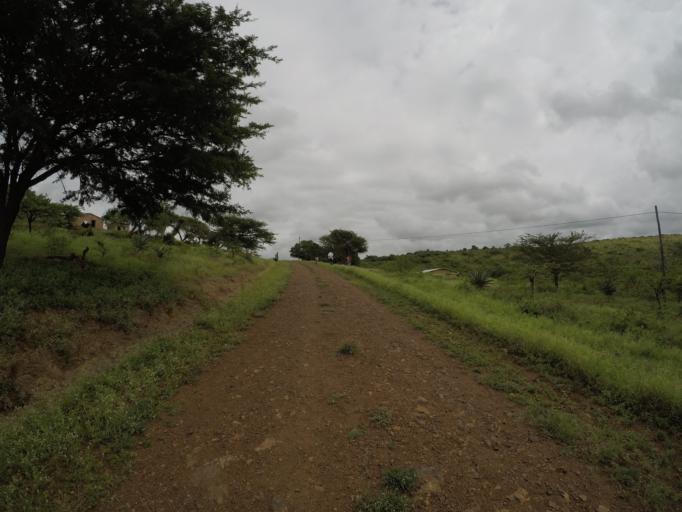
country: ZA
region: KwaZulu-Natal
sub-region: uThungulu District Municipality
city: Empangeni
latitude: -28.6276
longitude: 31.8903
